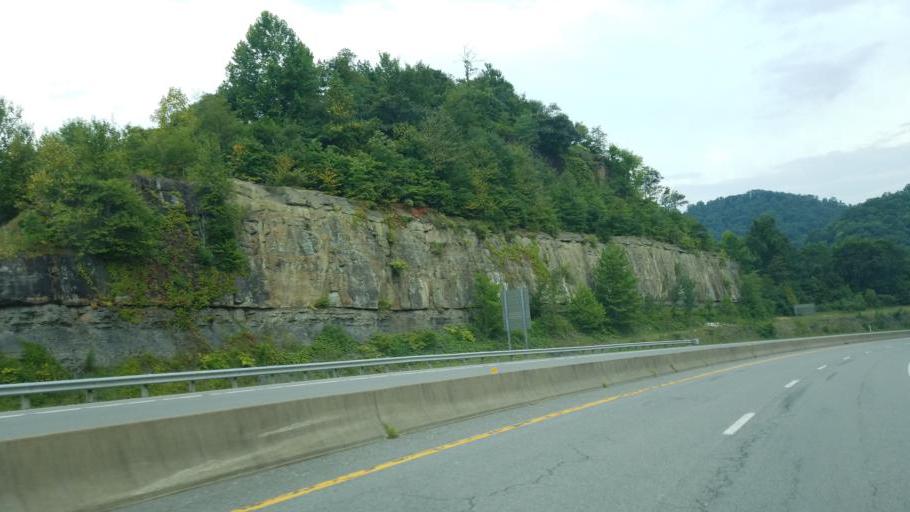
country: US
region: West Virginia
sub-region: Logan County
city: Mount Gay-Shamrock
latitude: 37.8331
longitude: -82.0460
